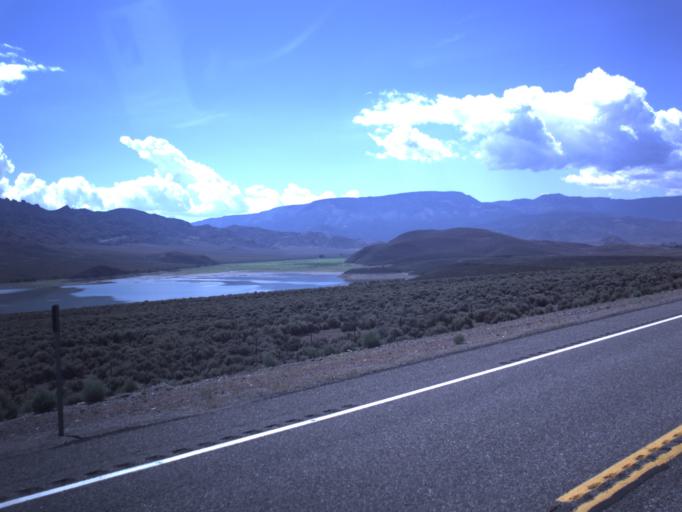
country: US
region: Utah
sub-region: Piute County
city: Junction
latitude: 38.3011
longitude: -112.2243
